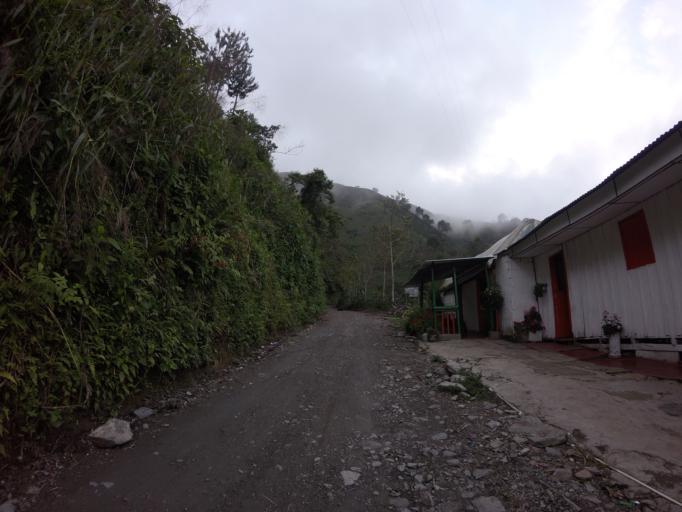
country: CO
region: Caldas
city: Marquetalia
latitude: 5.3554
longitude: -75.0715
